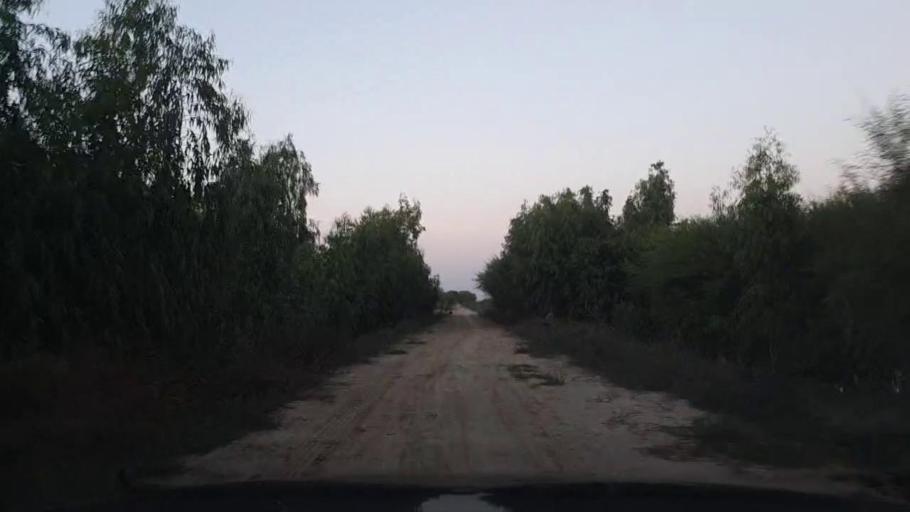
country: PK
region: Sindh
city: Thatta
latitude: 24.7427
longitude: 67.9571
